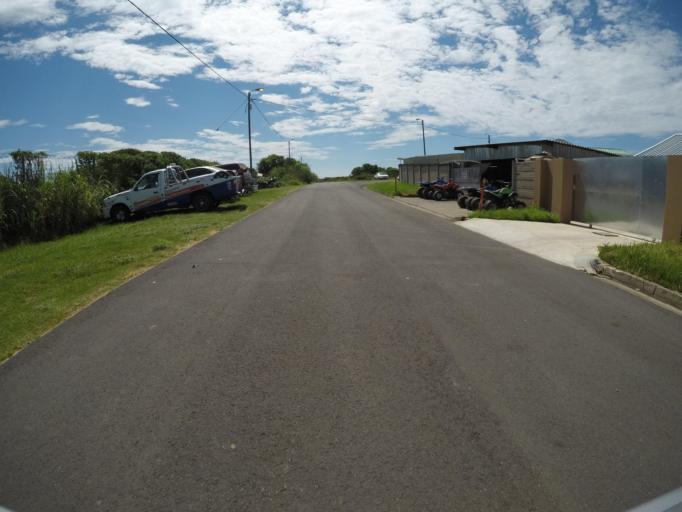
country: ZA
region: Eastern Cape
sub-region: Buffalo City Metropolitan Municipality
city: East London
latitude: -33.0387
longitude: 27.8837
